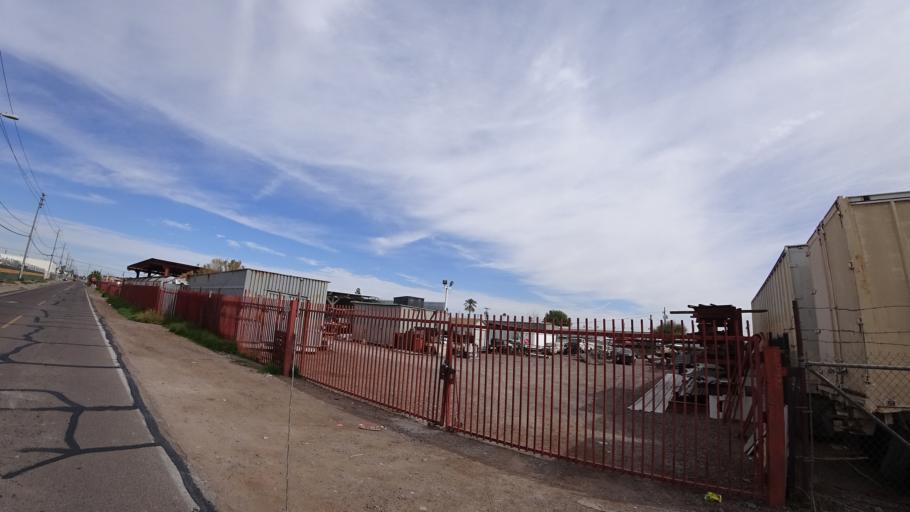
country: US
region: Arizona
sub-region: Maricopa County
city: Phoenix
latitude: 33.4410
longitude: -112.1260
